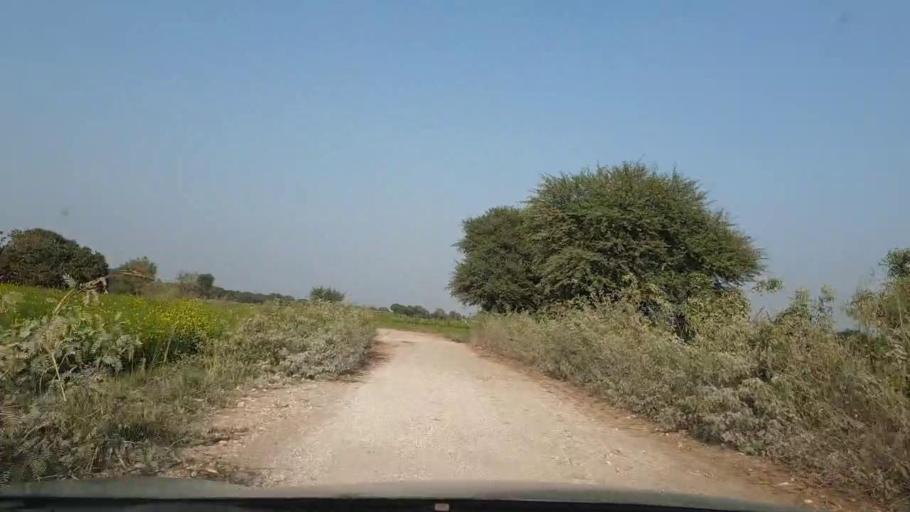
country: PK
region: Sindh
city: Tando Allahyar
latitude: 25.5583
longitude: 68.7938
